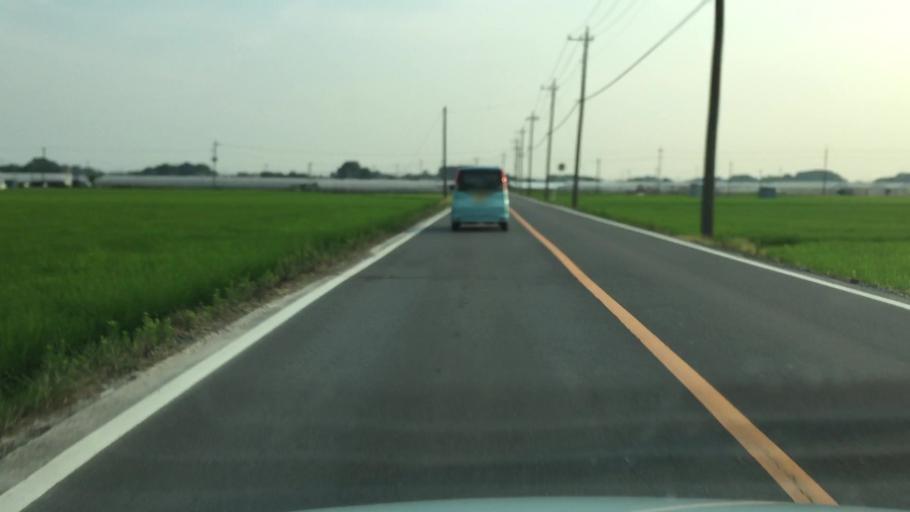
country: JP
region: Tochigi
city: Fujioka
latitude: 36.2426
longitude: 139.5961
